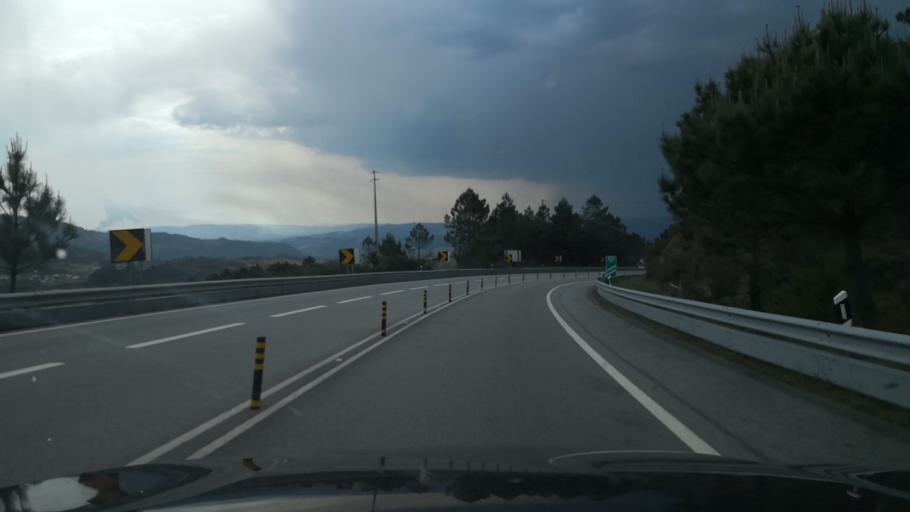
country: PT
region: Porto
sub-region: Baiao
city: Valadares
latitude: 41.2560
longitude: -7.9669
